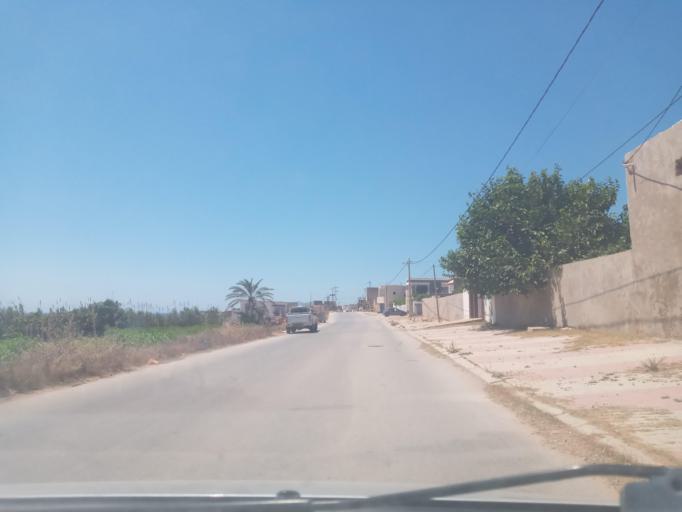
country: TN
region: Nabul
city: El Haouaria
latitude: 37.0521
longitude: 10.9979
